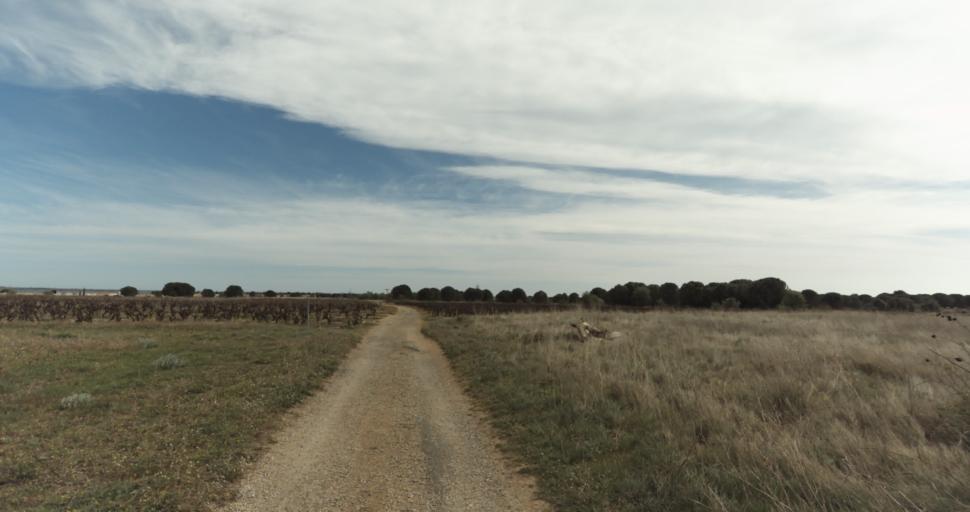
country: FR
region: Languedoc-Roussillon
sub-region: Departement de l'Herault
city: Marseillan
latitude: 43.3434
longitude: 3.5231
